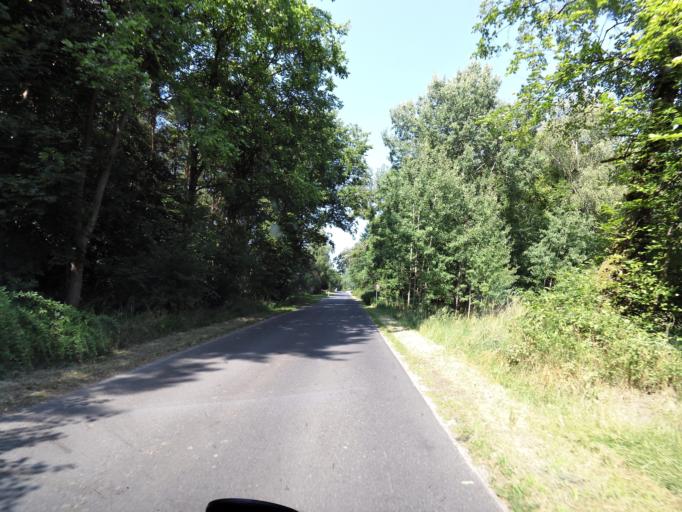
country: DE
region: Brandenburg
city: Zehdenick
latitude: 53.0222
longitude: 13.2920
